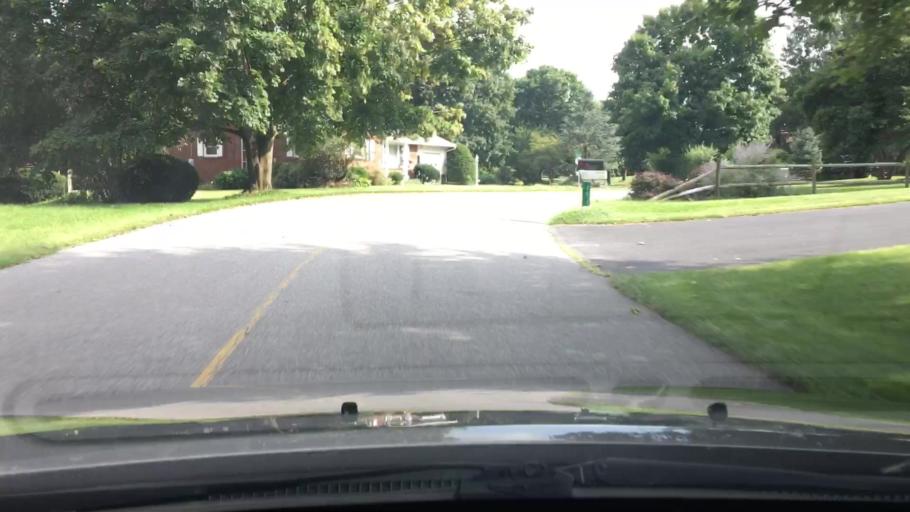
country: US
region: Pennsylvania
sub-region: Franklin County
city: Guilford
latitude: 39.9197
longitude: -77.5969
